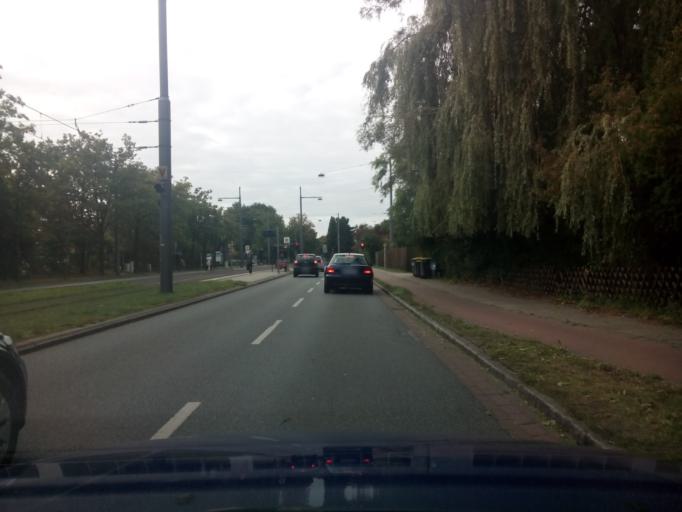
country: DE
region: Lower Saxony
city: Lilienthal
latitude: 53.1136
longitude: 8.8921
